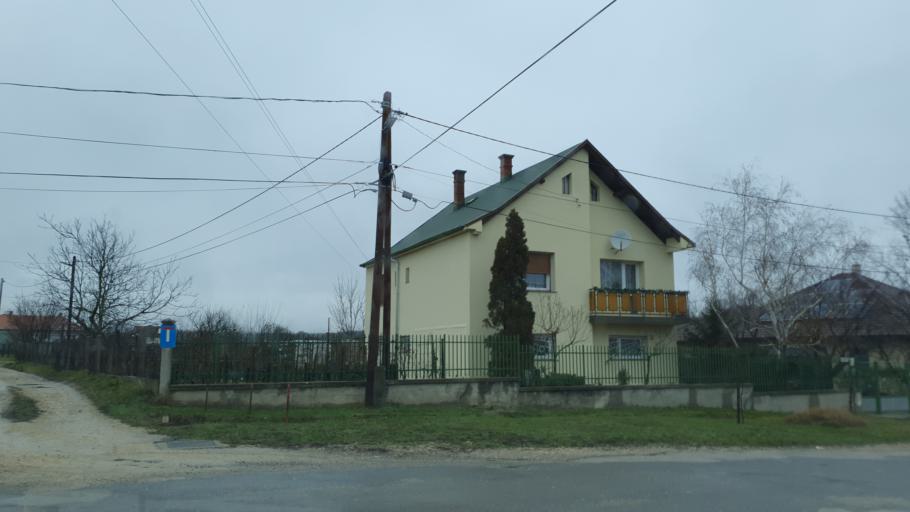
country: HU
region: Veszprem
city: Veszprem
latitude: 47.1438
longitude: 17.9419
